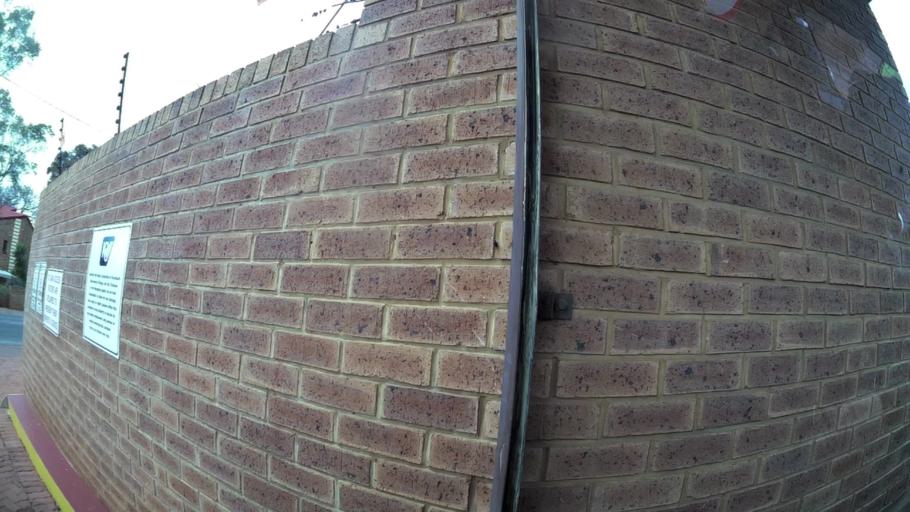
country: ZA
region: Gauteng
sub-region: City of Johannesburg Metropolitan Municipality
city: Roodepoort
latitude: -26.1112
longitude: 27.8578
